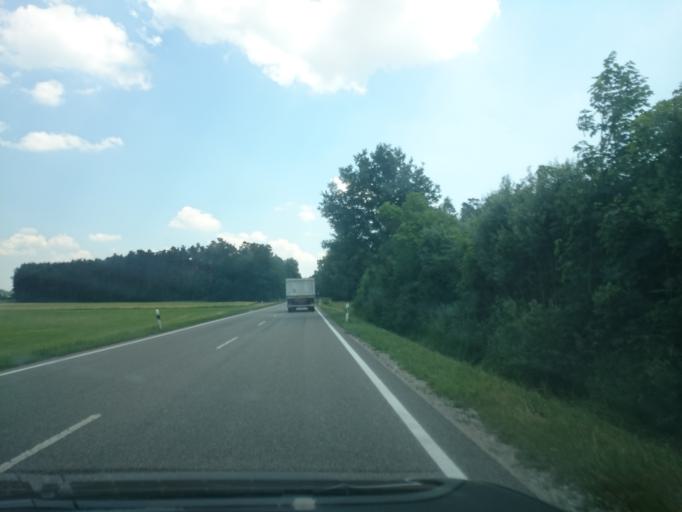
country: DE
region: Bavaria
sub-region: Regierungsbezirk Mittelfranken
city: Hilpoltstein
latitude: 49.2032
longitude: 11.1654
